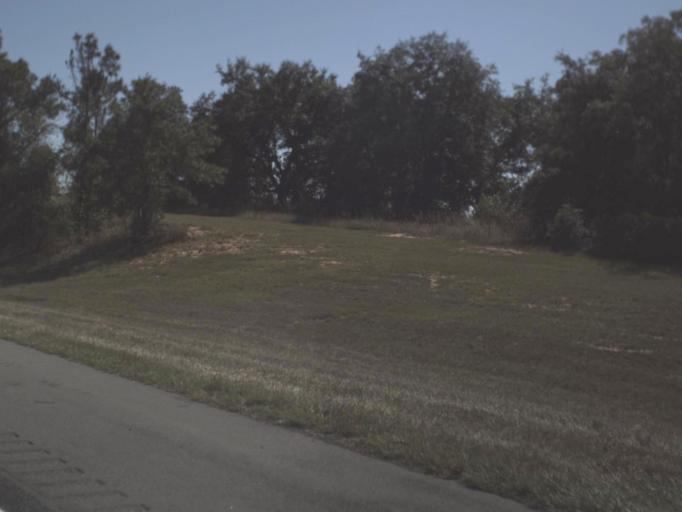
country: US
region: Florida
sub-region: Lake County
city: Minneola
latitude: 28.6334
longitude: -81.7747
